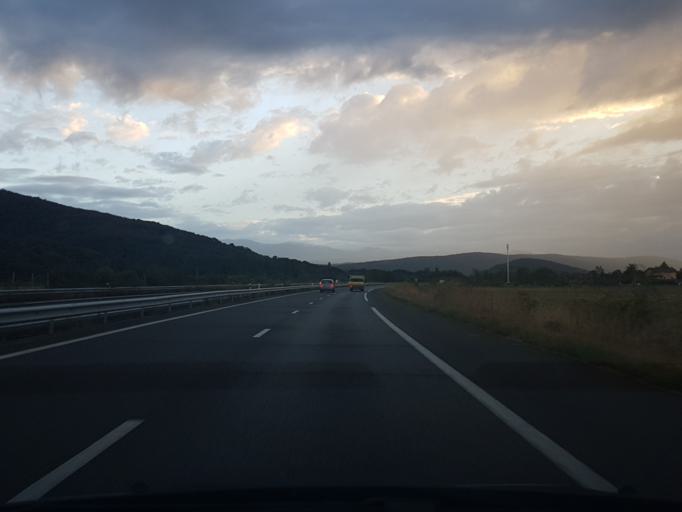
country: FR
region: Midi-Pyrenees
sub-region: Departement de l'Ariege
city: Varilhes
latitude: 43.0438
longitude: 1.6437
